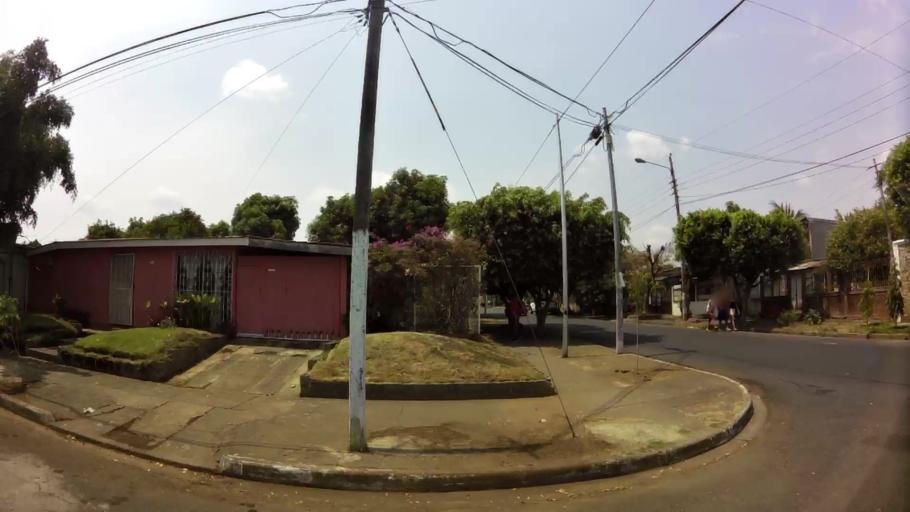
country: NI
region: Managua
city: Ciudad Sandino
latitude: 12.1522
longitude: -86.3139
